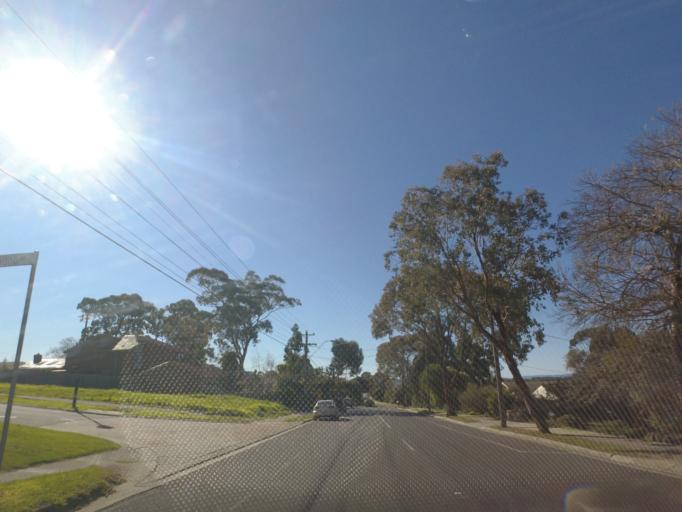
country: AU
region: Victoria
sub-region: Maroondah
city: Croydon Hills
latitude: -37.7787
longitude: 145.2565
